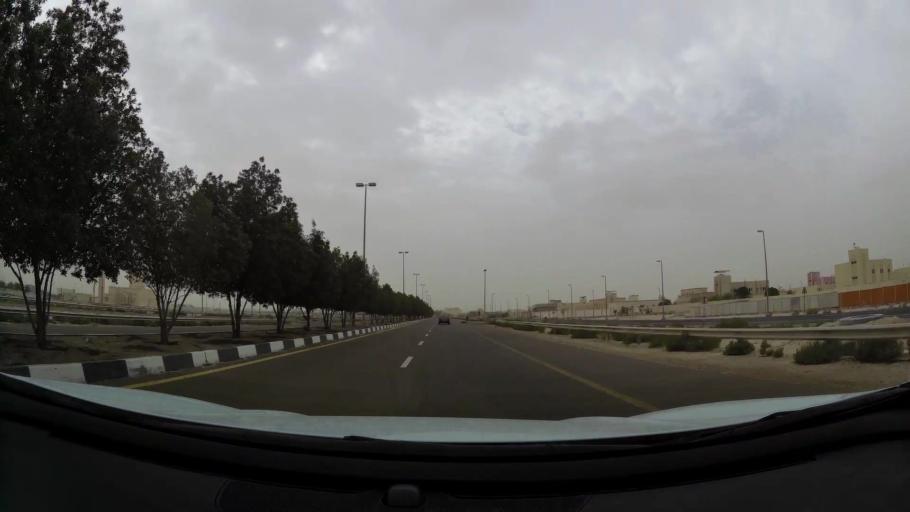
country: AE
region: Abu Dhabi
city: Abu Dhabi
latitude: 24.3833
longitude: 54.7057
